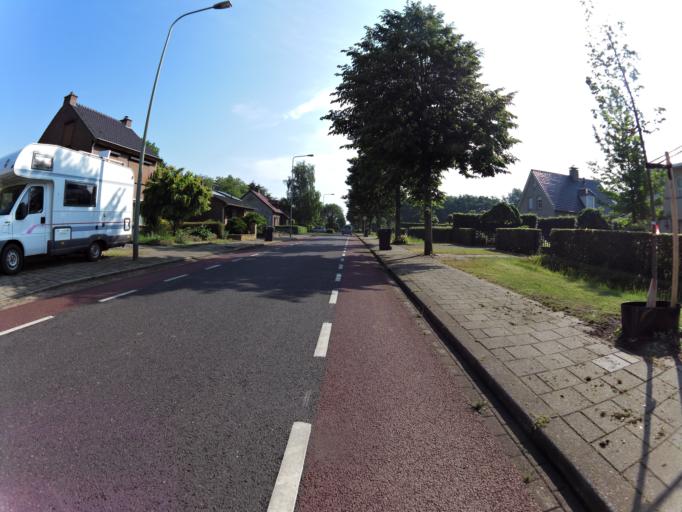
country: NL
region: Limburg
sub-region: Gemeente Maasgouw
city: Maasbracht
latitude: 51.0710
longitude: 5.8782
